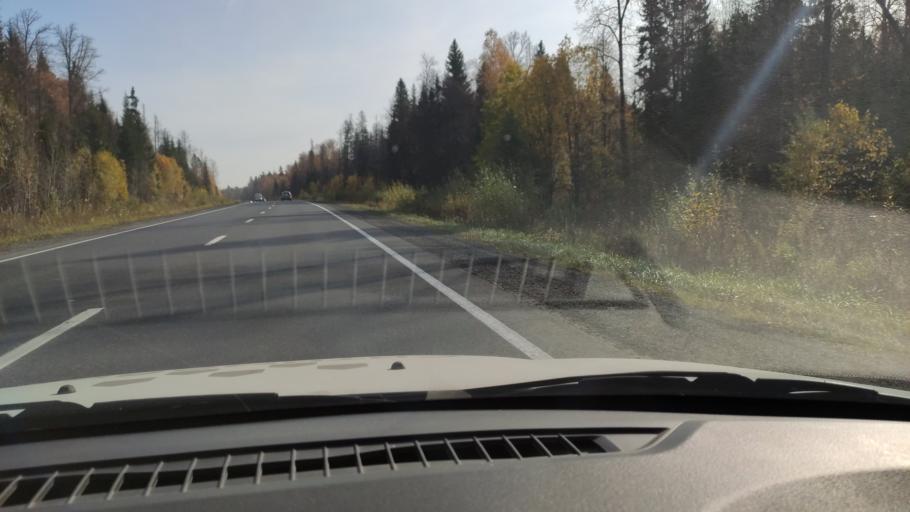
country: RU
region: Perm
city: Novyye Lyady
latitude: 58.0299
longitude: 56.4901
